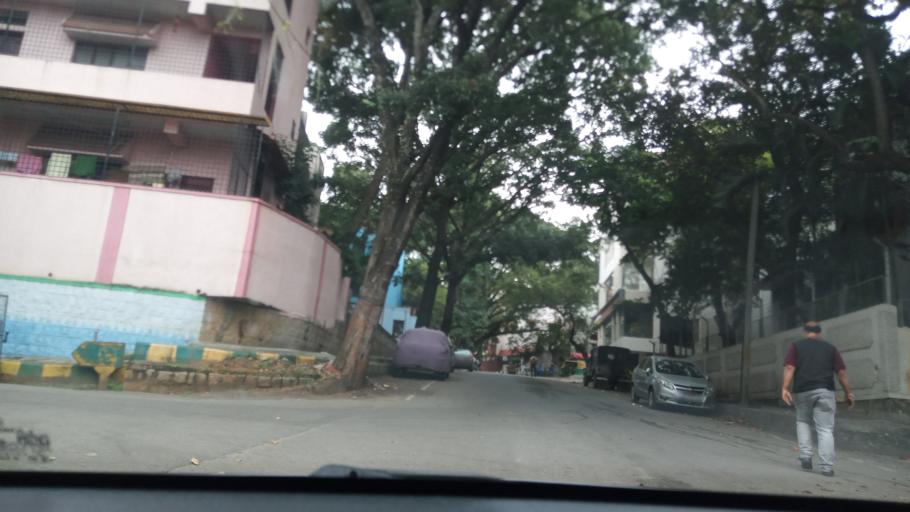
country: IN
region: Karnataka
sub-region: Bangalore Urban
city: Bangalore
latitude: 13.0104
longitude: 77.5382
